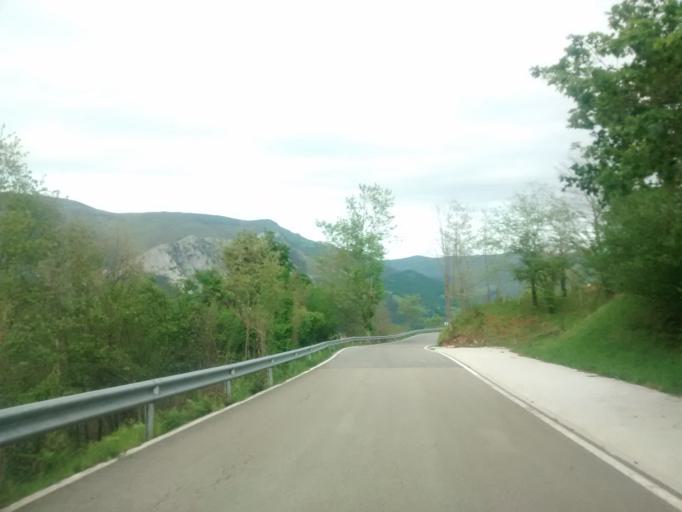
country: ES
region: Cantabria
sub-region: Provincia de Cantabria
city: San Vicente de la Barquera
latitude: 43.2537
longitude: -4.4361
